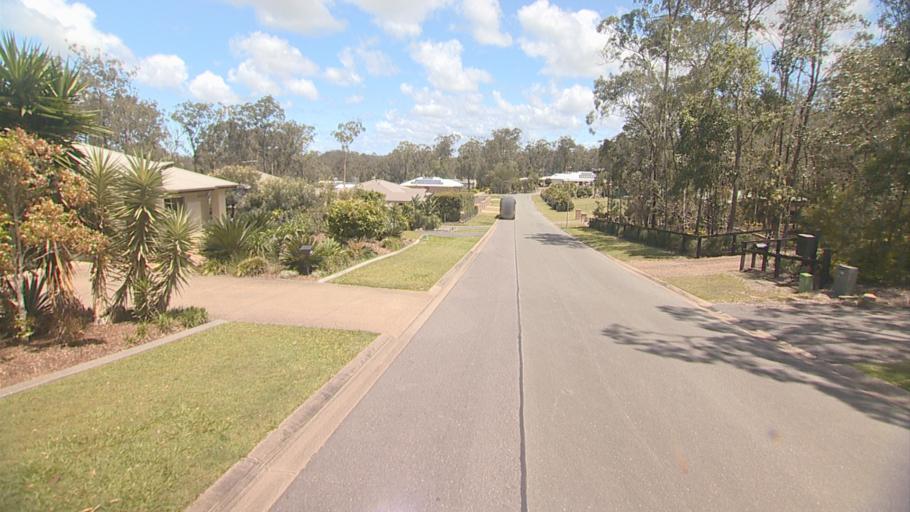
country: AU
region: Queensland
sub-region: Logan
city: Beenleigh
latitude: -27.6678
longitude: 153.2268
